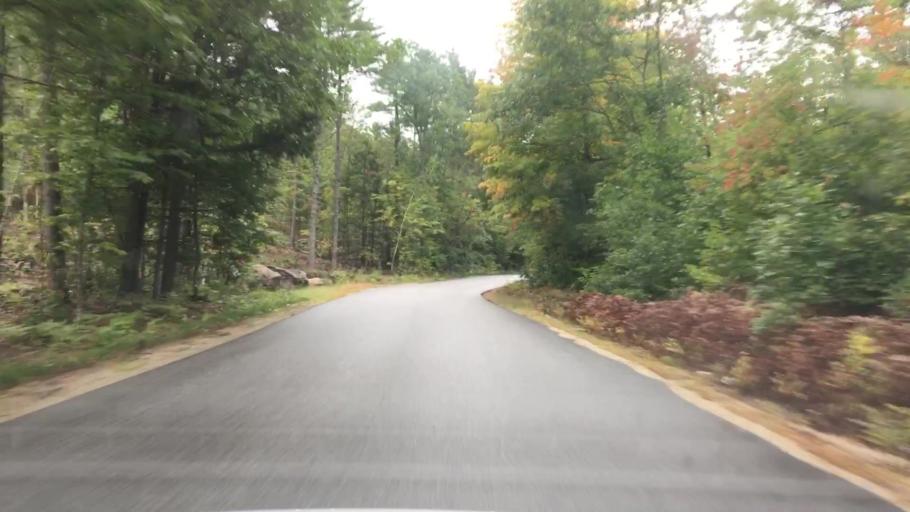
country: US
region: Maine
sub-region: Cumberland County
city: Harrison
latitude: 44.0167
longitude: -70.5852
